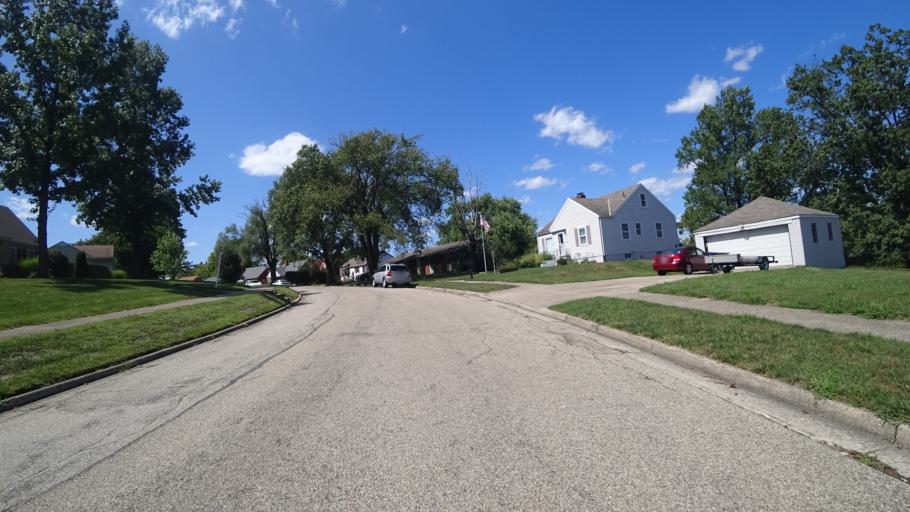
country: US
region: Ohio
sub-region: Butler County
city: New Miami
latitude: 39.4101
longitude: -84.5354
